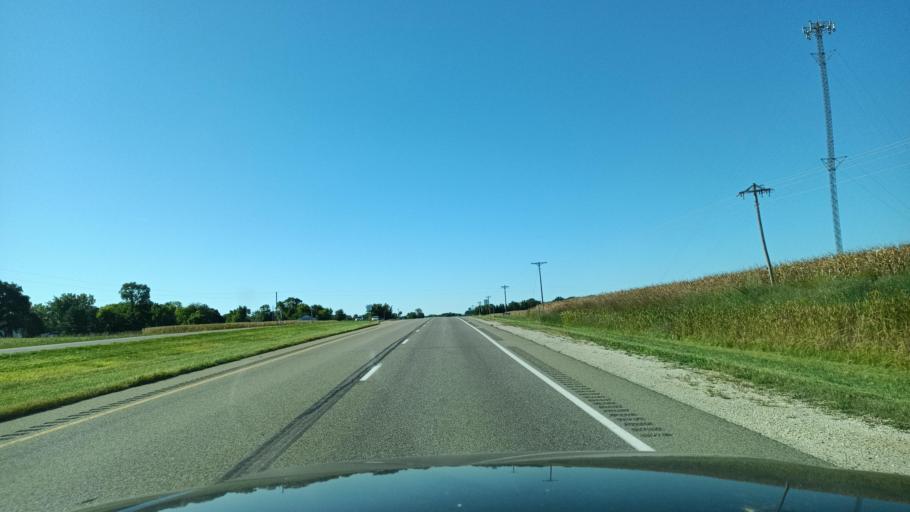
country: US
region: Iowa
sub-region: Lee County
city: Fort Madison
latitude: 40.6886
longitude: -91.2499
